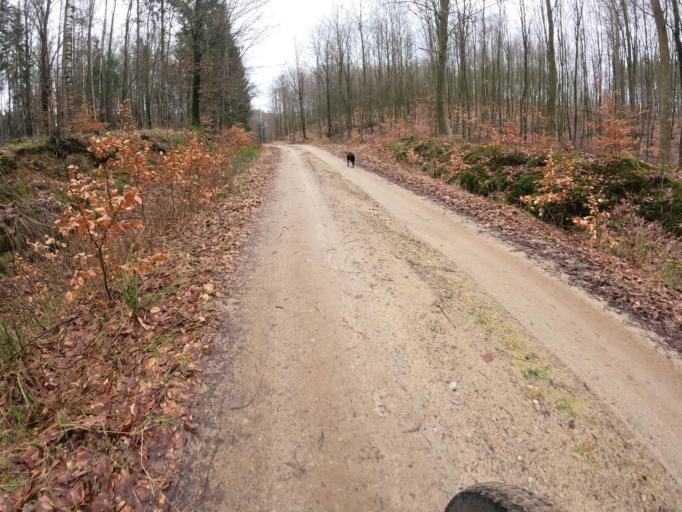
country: PL
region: West Pomeranian Voivodeship
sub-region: Powiat koszalinski
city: Polanow
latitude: 54.2315
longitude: 16.6794
